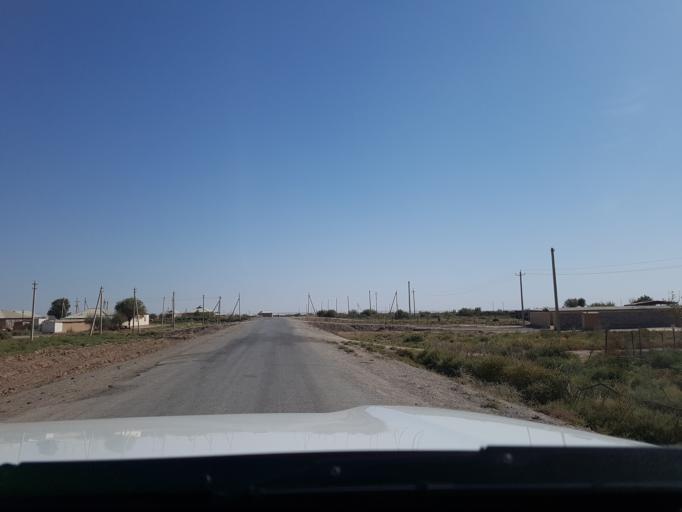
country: IR
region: Razavi Khorasan
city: Sarakhs
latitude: 36.5173
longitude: 61.2515
